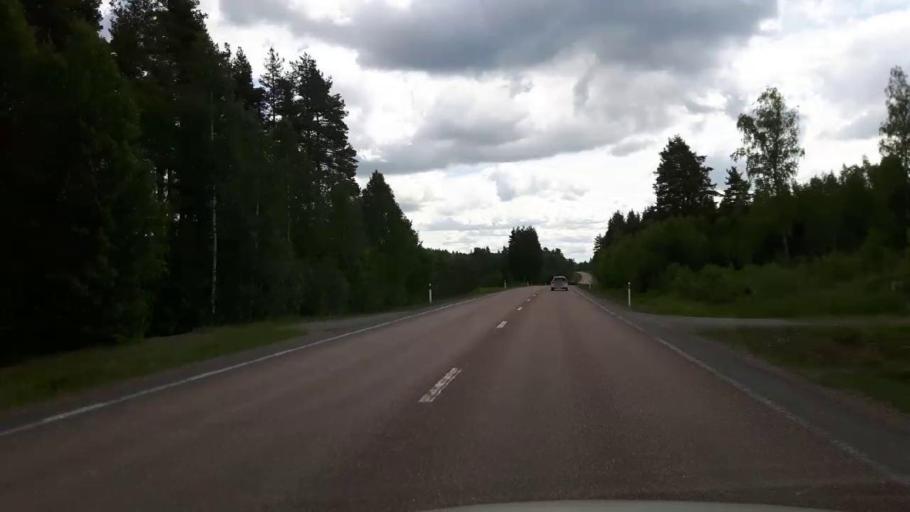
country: SE
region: Dalarna
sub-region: Saters Kommun
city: Saeter
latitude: 60.4903
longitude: 15.7643
